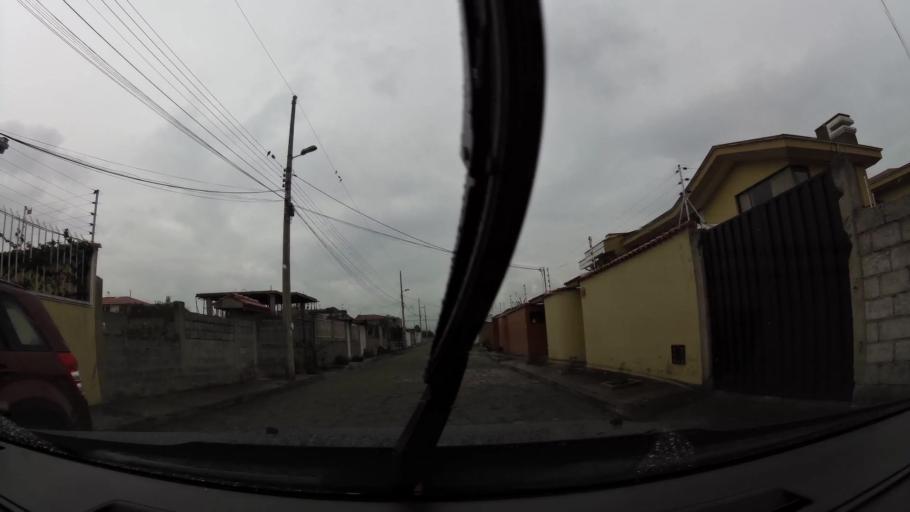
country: EC
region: Pichincha
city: Sangolqui
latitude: -0.3205
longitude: -78.4325
